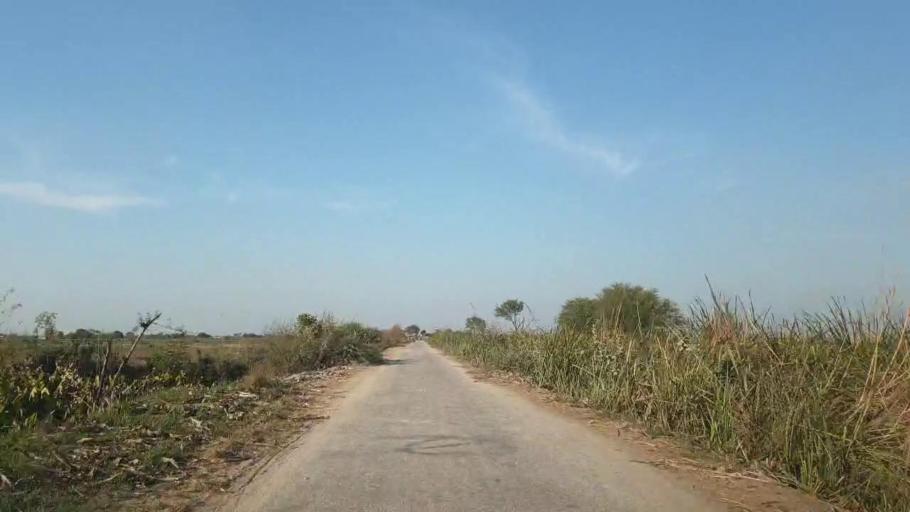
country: PK
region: Sindh
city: Tando Adam
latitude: 25.7267
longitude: 68.7027
